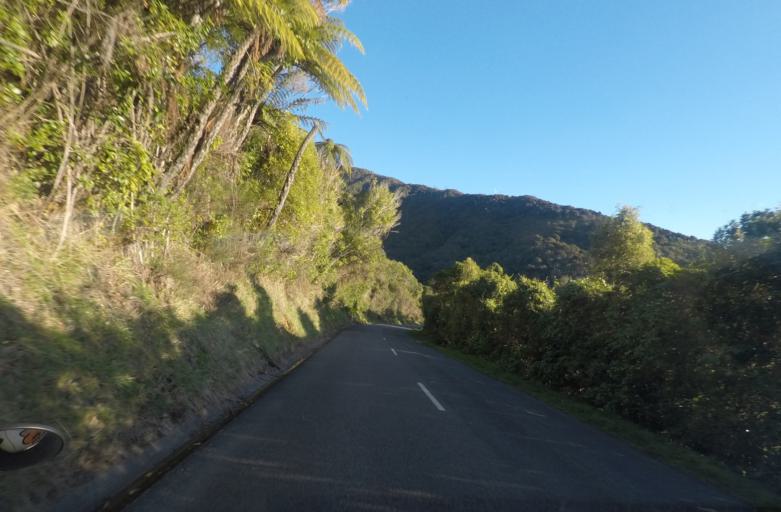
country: NZ
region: Marlborough
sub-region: Marlborough District
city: Picton
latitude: -41.2695
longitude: 173.9432
